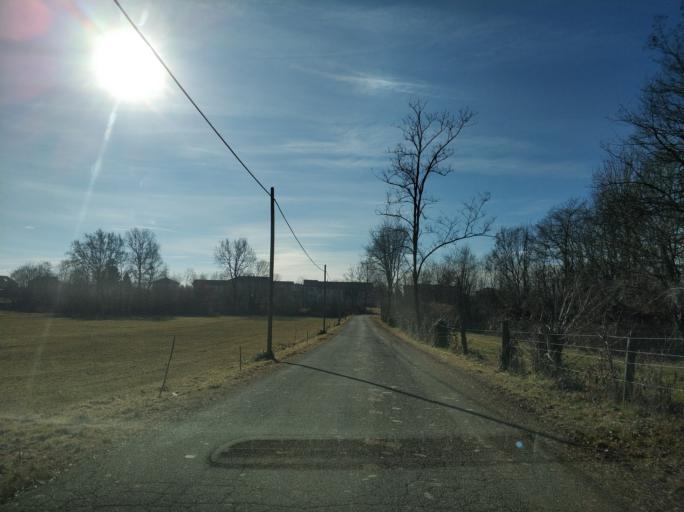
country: IT
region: Piedmont
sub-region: Provincia di Torino
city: San Carlo Canavese
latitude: 45.2531
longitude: 7.5990
